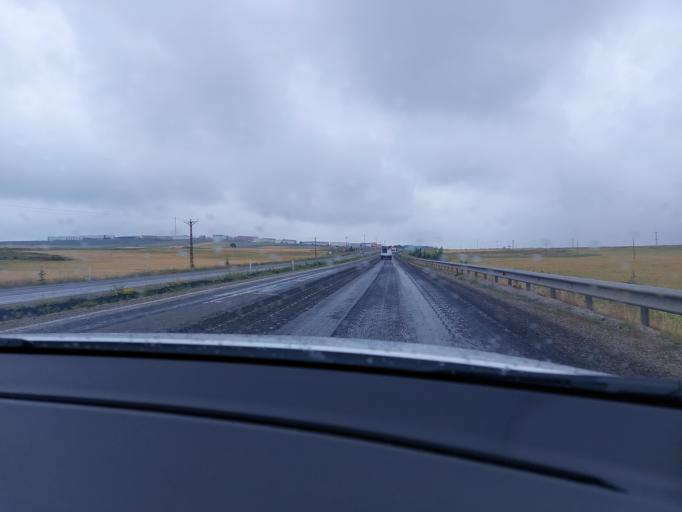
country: TR
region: Nevsehir
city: Dobada
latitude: 38.5372
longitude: 34.4502
